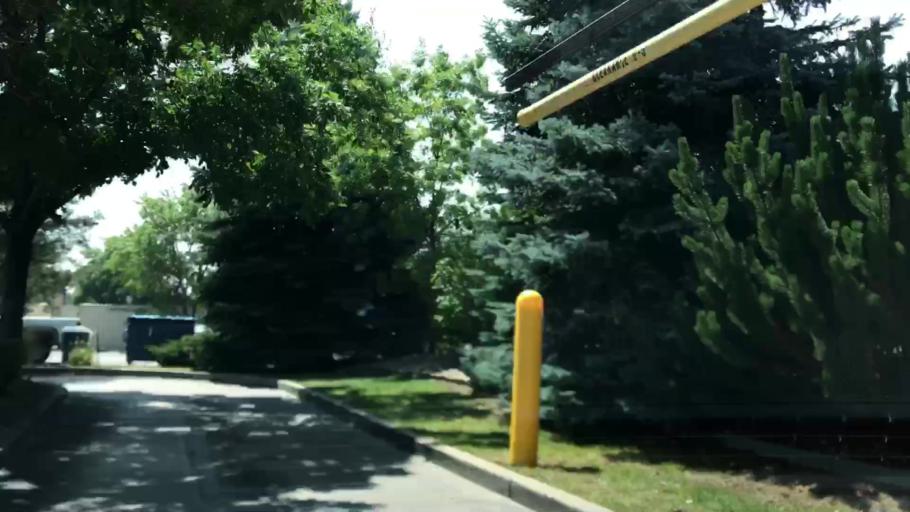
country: US
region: Colorado
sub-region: Boulder County
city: Boulder
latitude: 40.0338
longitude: -105.2596
